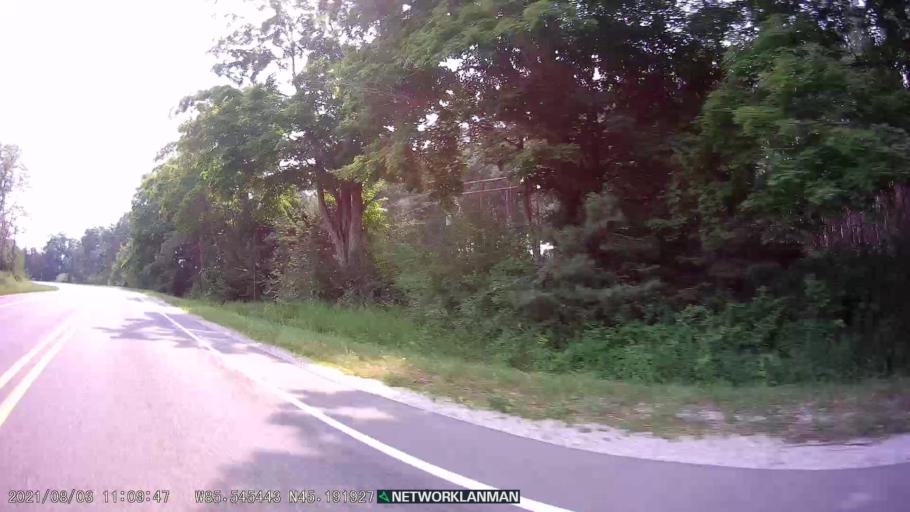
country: US
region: Michigan
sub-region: Leelanau County
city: Leland
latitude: 45.1917
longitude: -85.5454
